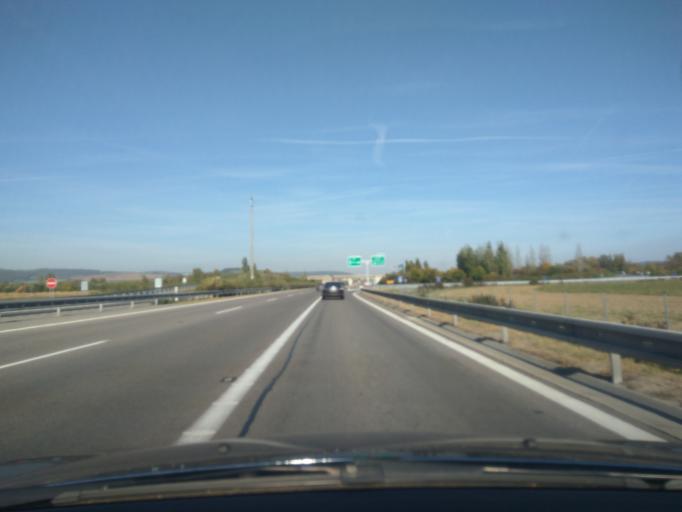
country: SK
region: Trenciansky
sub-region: Okres Trencin
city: Trencin
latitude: 48.8573
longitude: 17.9544
